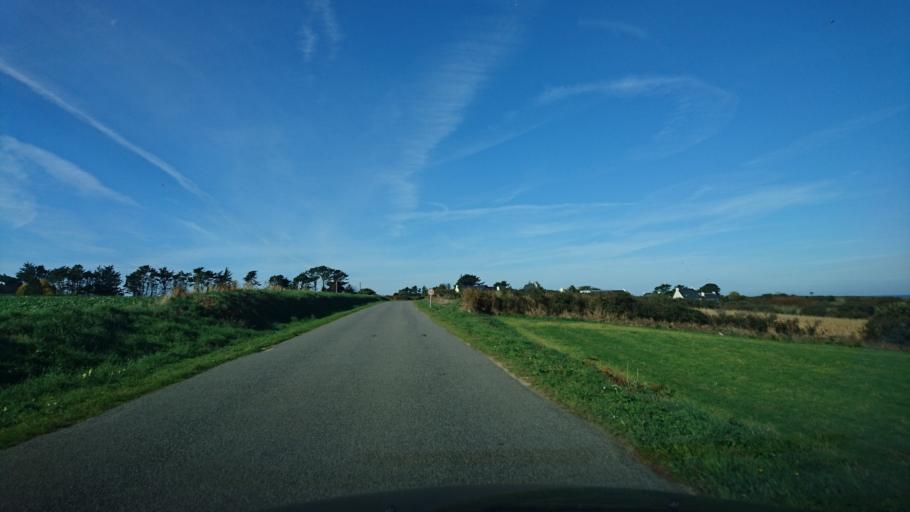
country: FR
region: Brittany
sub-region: Departement du Finistere
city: Lampaul-Plouarzel
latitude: 48.4308
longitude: -4.7650
